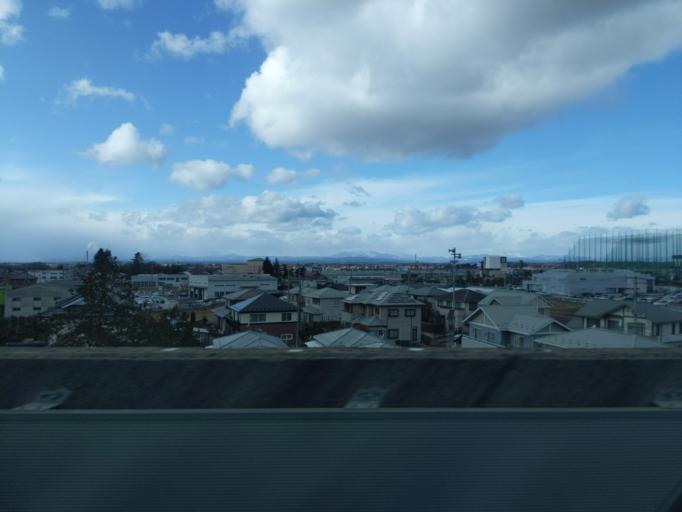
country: JP
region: Miyagi
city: Furukawa
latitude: 38.5955
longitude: 140.9791
